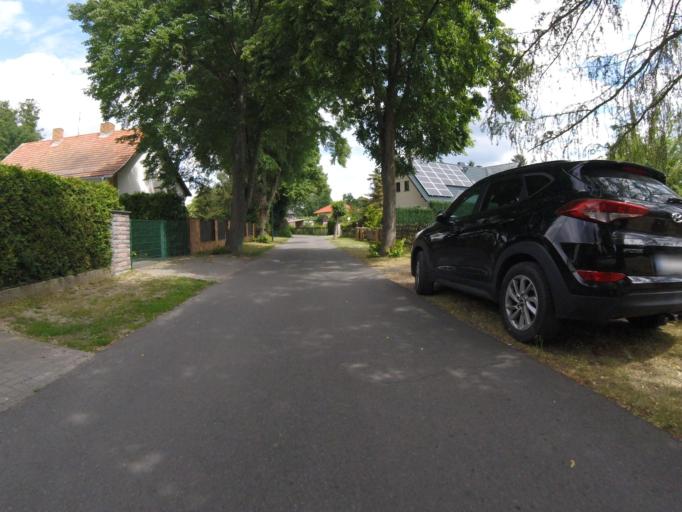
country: DE
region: Brandenburg
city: Halbe
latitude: 52.1106
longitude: 13.6956
